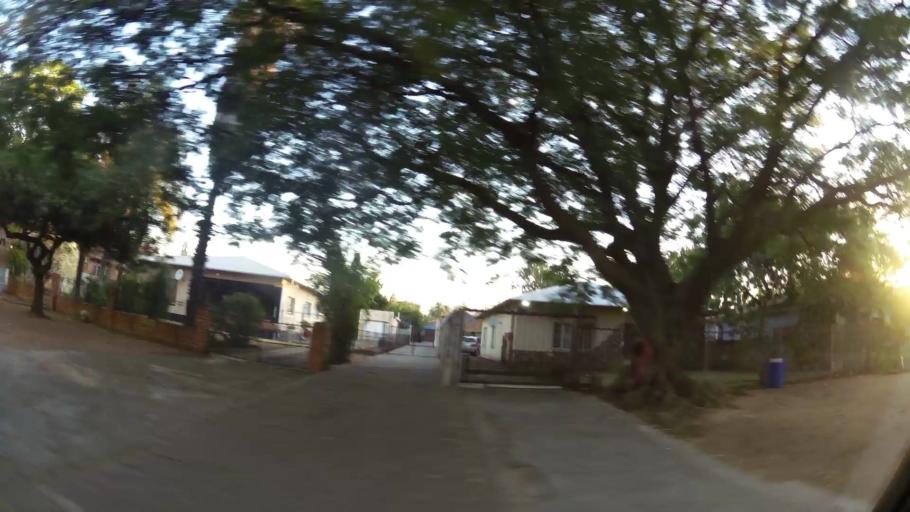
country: ZA
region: North-West
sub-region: Bojanala Platinum District Municipality
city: Rustenburg
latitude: -25.6708
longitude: 27.2280
